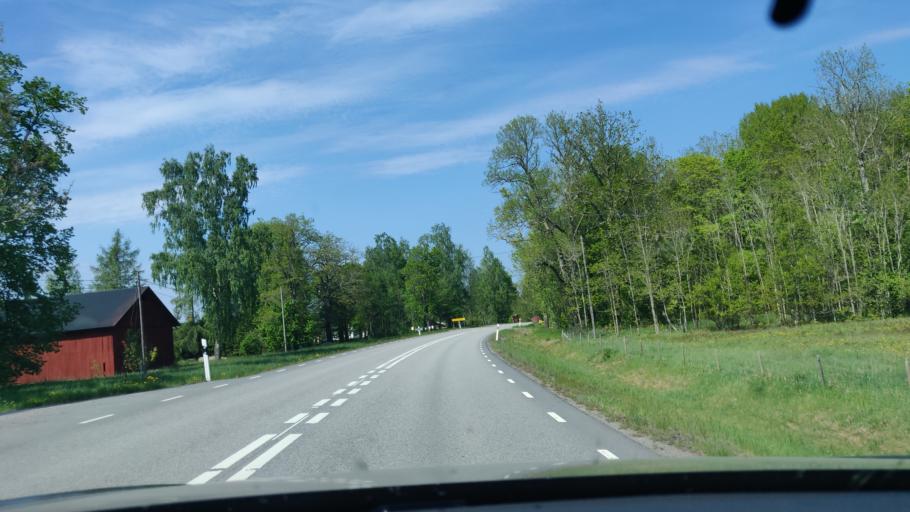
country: SE
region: Uppsala
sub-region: Heby Kommun
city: OEstervala
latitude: 60.1495
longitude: 17.1997
